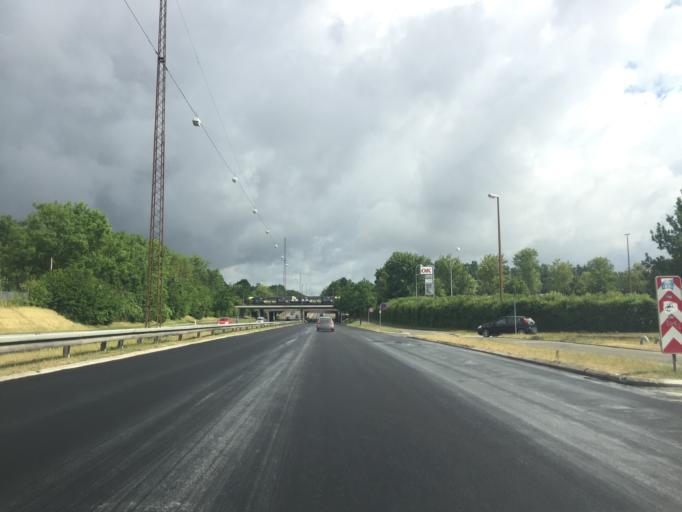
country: DK
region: Capital Region
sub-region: Rodovre Kommune
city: Rodovre
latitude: 55.6624
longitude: 12.4550
